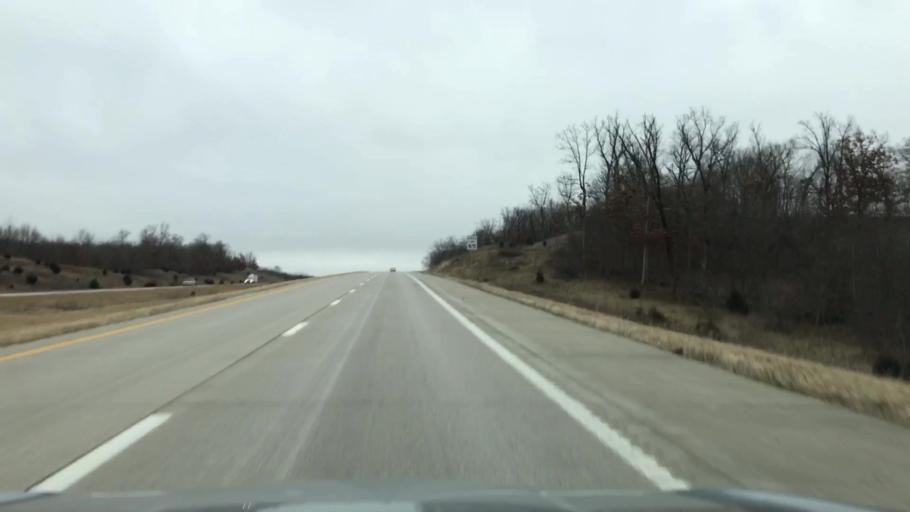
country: US
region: Missouri
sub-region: Linn County
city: Marceline
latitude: 39.7588
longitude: -92.8518
